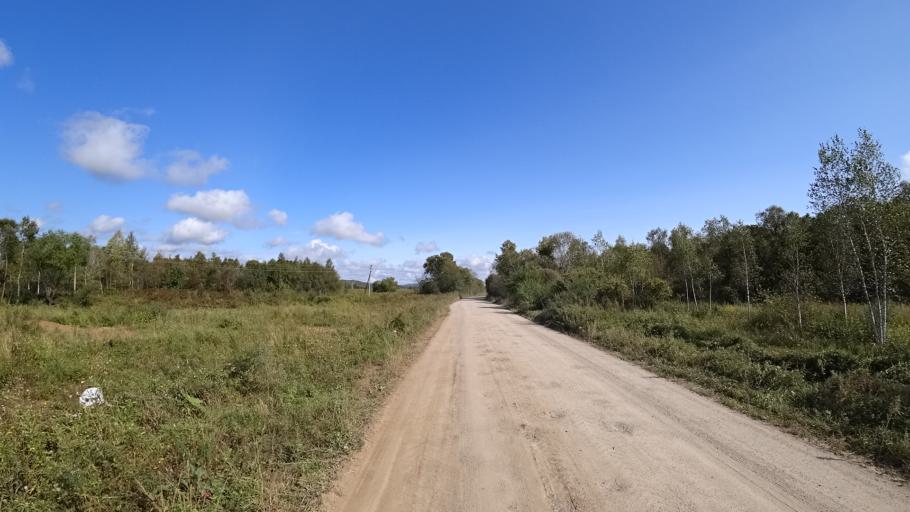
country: RU
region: Amur
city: Arkhara
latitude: 49.4096
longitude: 130.1624
